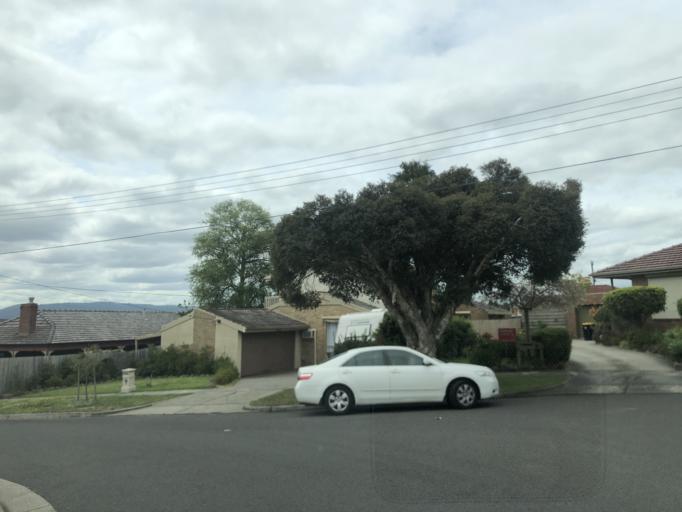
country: AU
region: Victoria
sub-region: Greater Dandenong
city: Dandenong North
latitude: -37.9489
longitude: 145.2177
